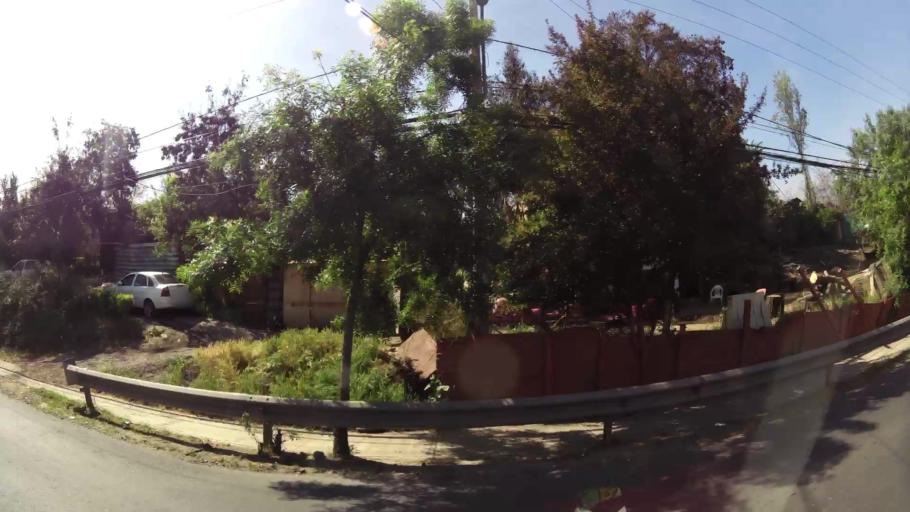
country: CL
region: Santiago Metropolitan
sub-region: Provincia de Cordillera
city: Puente Alto
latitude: -33.5362
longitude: -70.5586
